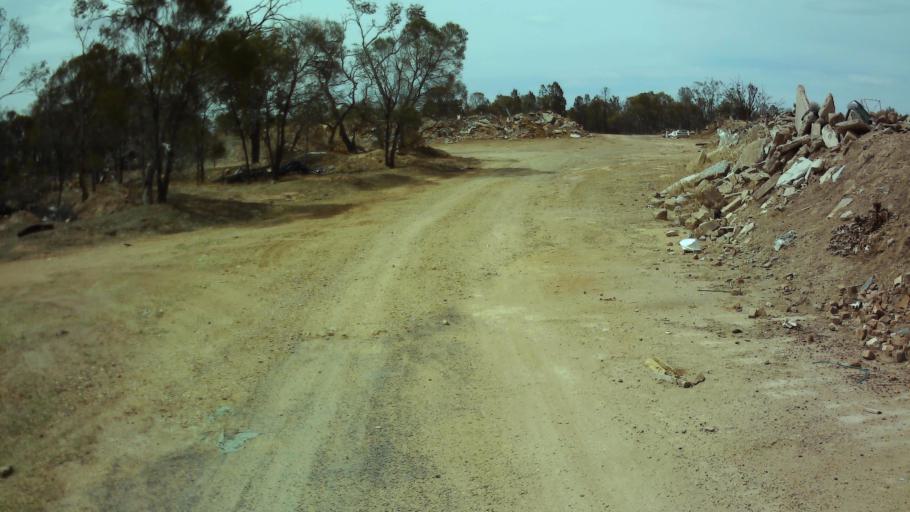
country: AU
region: New South Wales
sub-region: Weddin
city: Grenfell
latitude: -33.8681
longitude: 148.1660
